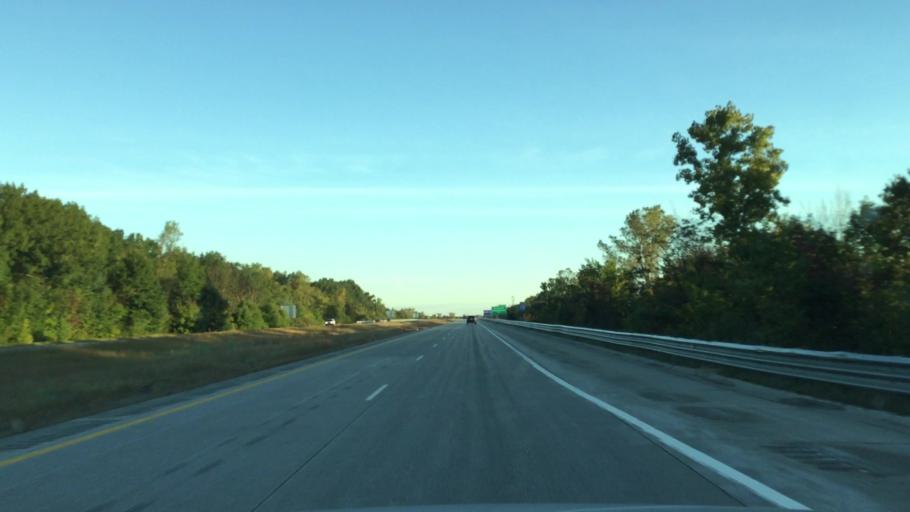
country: US
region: Michigan
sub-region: Genesee County
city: Grand Blanc
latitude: 42.9516
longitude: -83.6819
